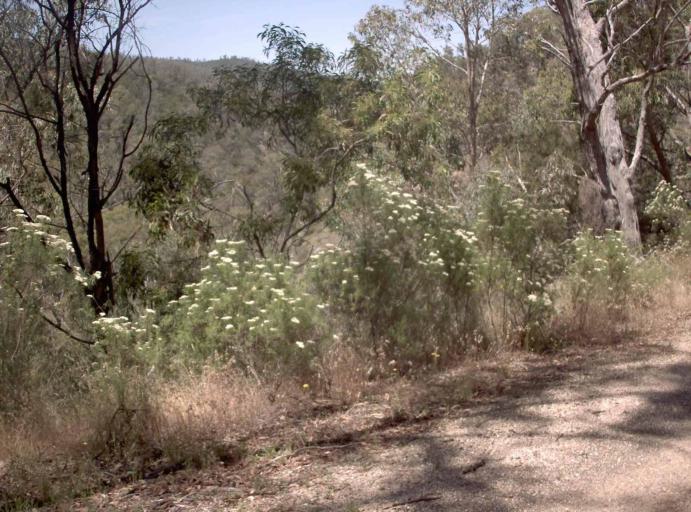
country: AU
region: Victoria
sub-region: East Gippsland
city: Bairnsdale
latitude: -37.4244
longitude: 147.8317
